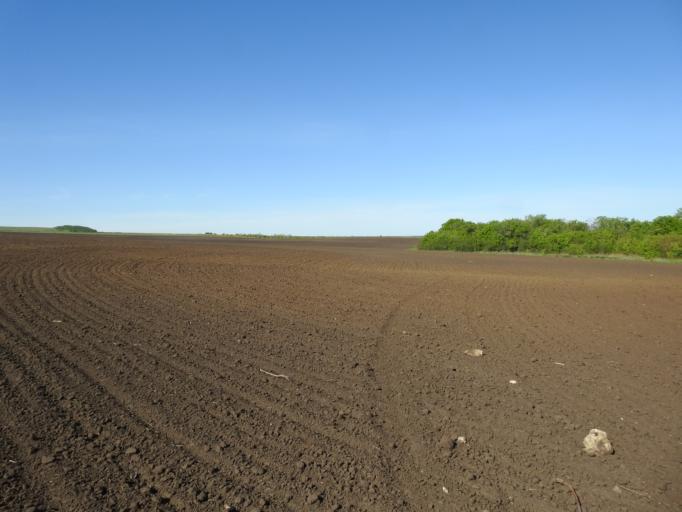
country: RU
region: Saratov
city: Krasnyy Oktyabr'
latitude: 51.6215
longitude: 45.7369
